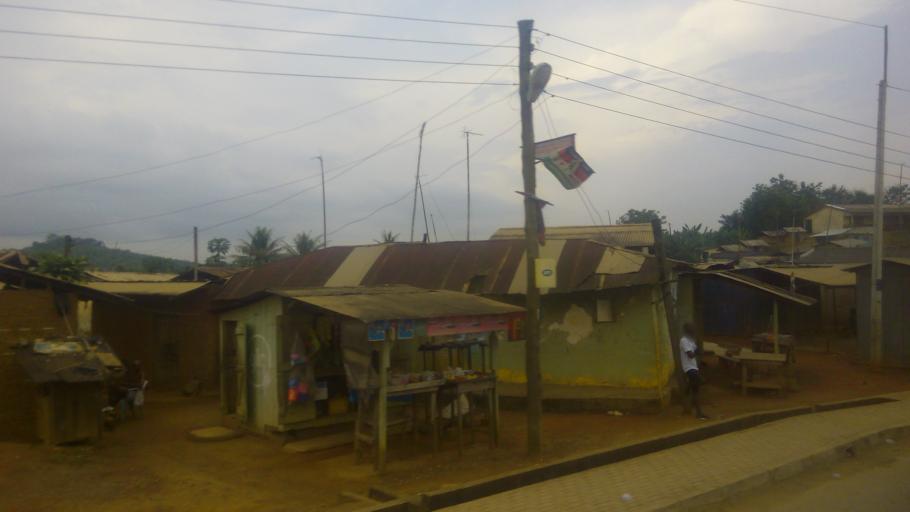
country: GH
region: Western
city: Takoradi
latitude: 4.8927
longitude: -1.8828
